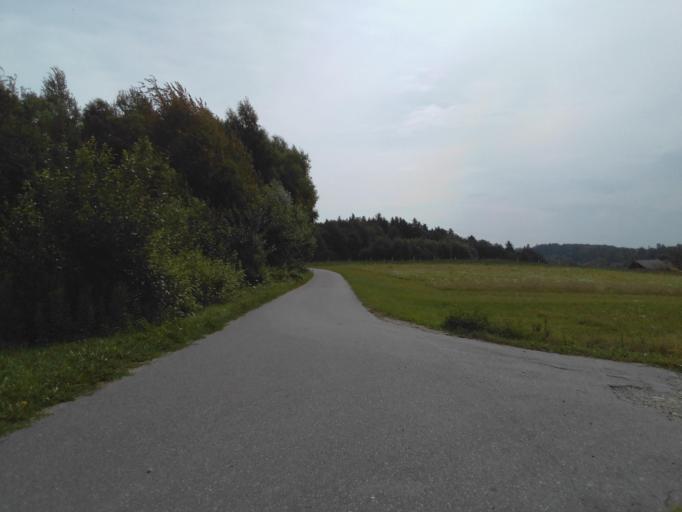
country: PL
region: Subcarpathian Voivodeship
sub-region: Powiat strzyzowski
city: Frysztak
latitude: 49.8656
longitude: 21.5810
